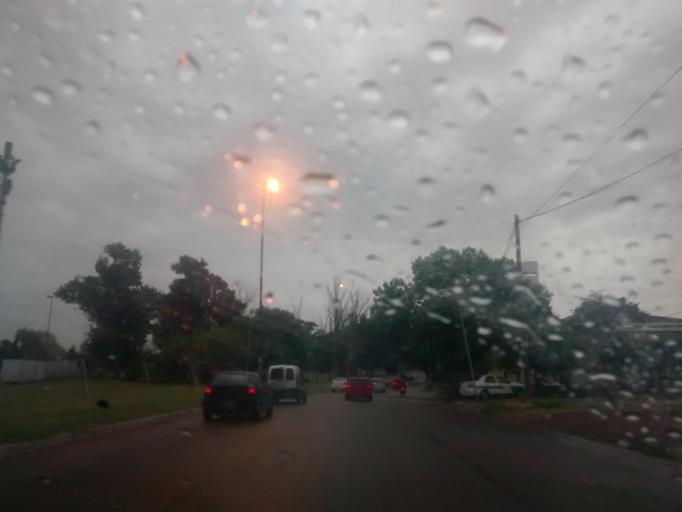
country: AR
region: Buenos Aires
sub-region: Partido de La Plata
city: La Plata
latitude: -34.9267
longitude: -57.9882
